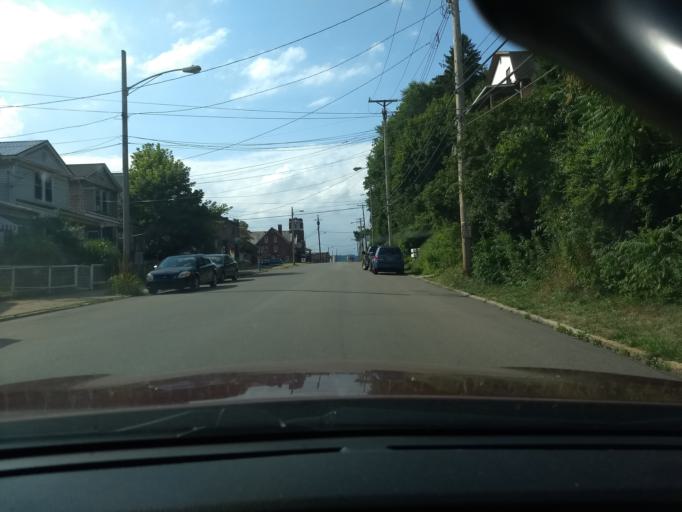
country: US
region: Pennsylvania
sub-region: Beaver County
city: Ambridge
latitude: 40.5804
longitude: -80.2228
